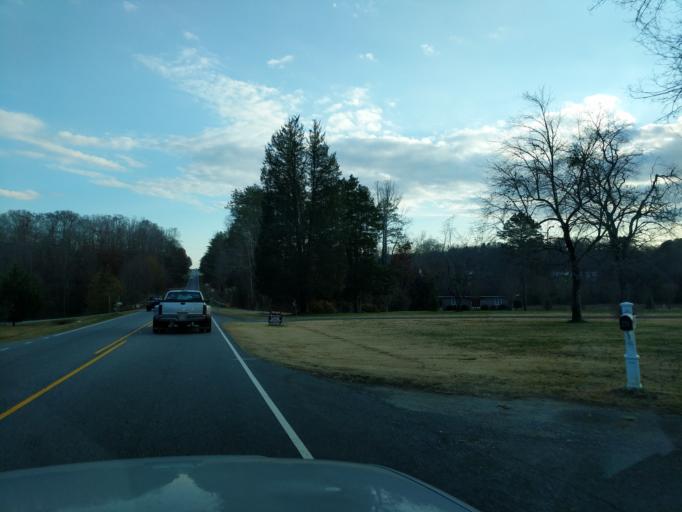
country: US
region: North Carolina
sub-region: Rutherford County
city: Rutherfordton
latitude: 35.3942
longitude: -81.9618
